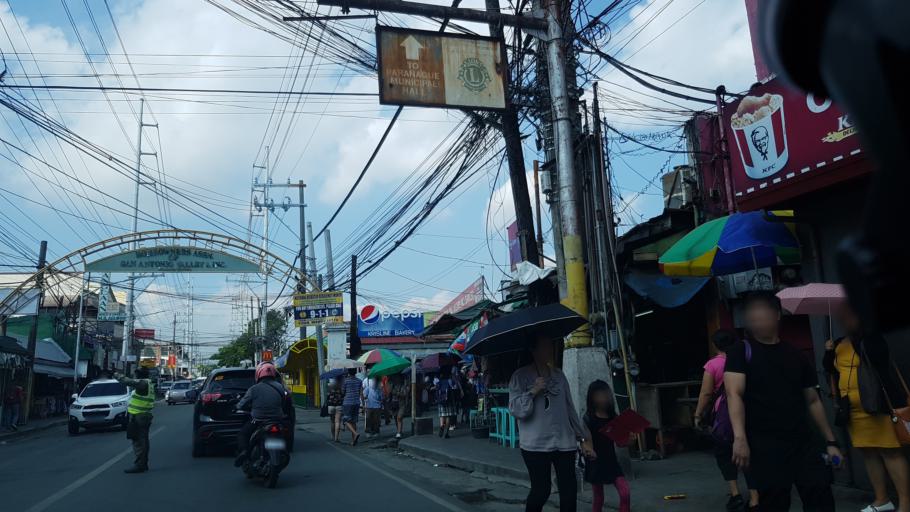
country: PH
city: Sambayanihan People's Village
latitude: 14.4650
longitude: 121.0199
